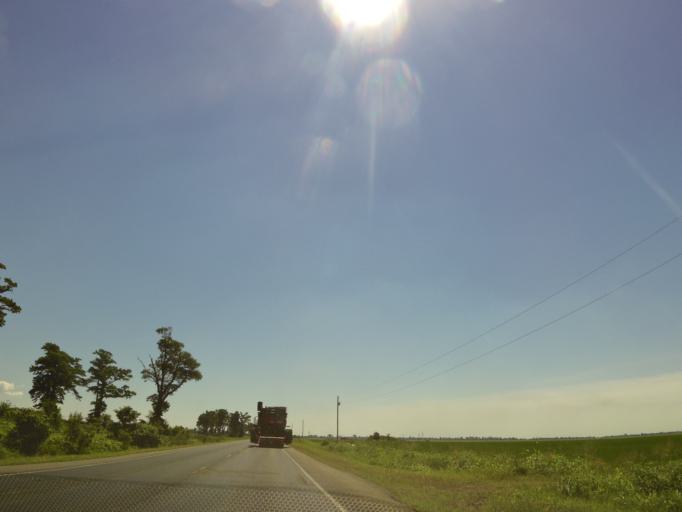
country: US
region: Missouri
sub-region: New Madrid County
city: Lilbourn
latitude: 36.5537
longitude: -89.7160
